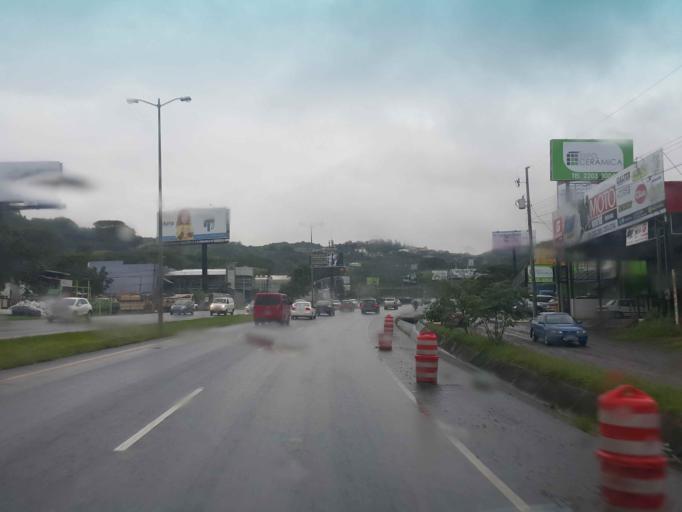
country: CR
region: San Jose
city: Santa Ana
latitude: 9.9467
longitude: -84.1847
